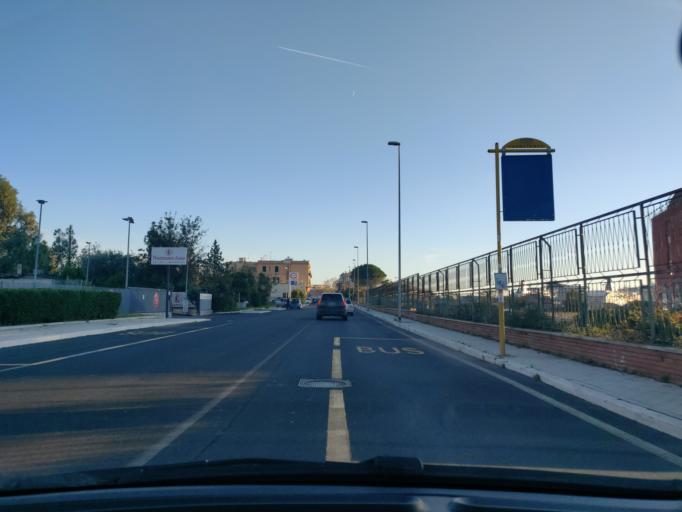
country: IT
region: Latium
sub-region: Citta metropolitana di Roma Capitale
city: Civitavecchia
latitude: 42.1031
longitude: 11.7865
